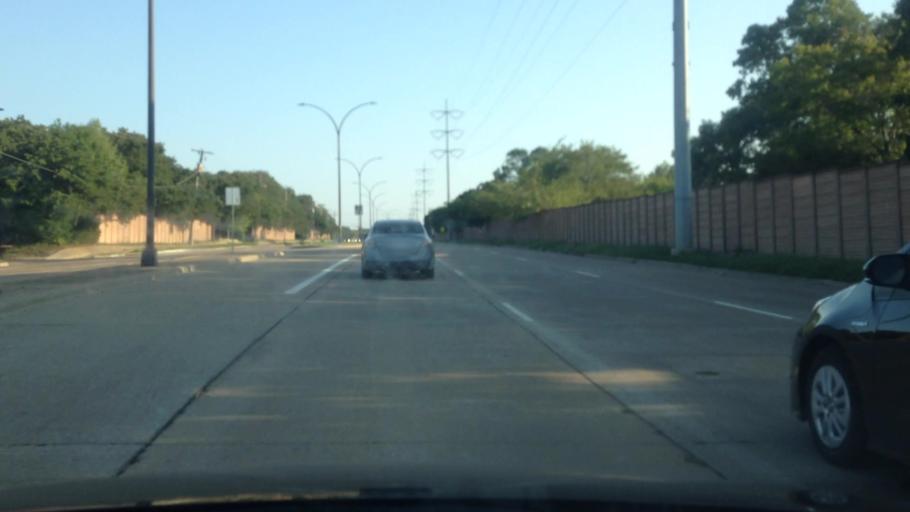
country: US
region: Texas
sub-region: Tarrant County
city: Dalworthington Gardens
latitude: 32.7004
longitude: -97.1903
